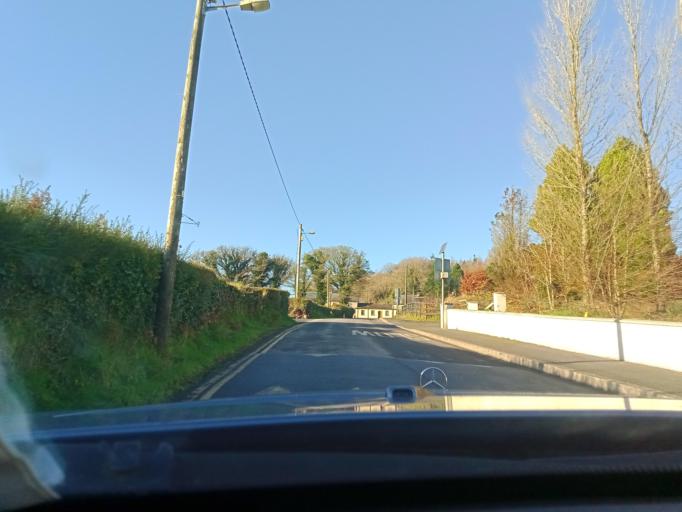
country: IE
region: Leinster
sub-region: Kilkenny
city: Callan
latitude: 52.4613
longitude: -7.3966
